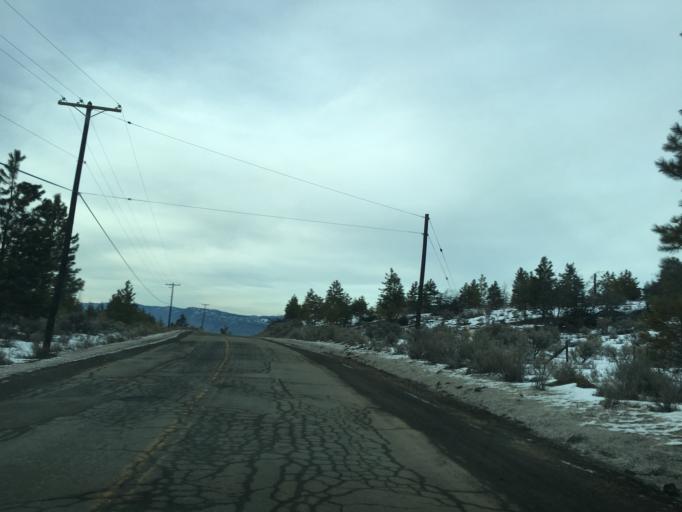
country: CA
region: British Columbia
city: Kamloops
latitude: 50.6473
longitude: -120.4516
